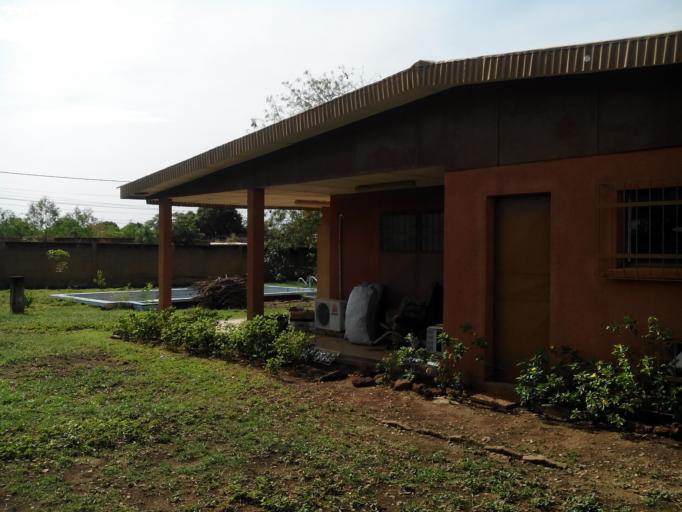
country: CI
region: Savanes
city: Korhogo
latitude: 9.4413
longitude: -5.6322
